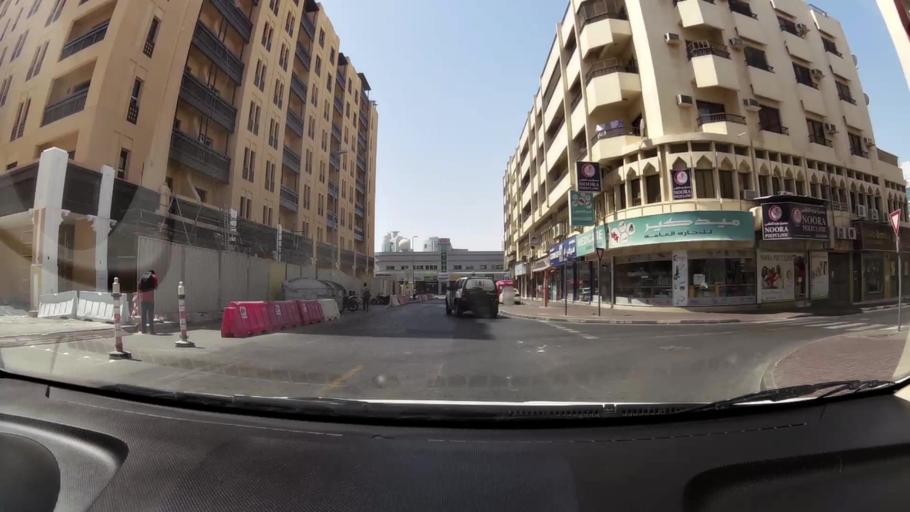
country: AE
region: Ash Shariqah
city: Sharjah
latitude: 25.2707
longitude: 55.3128
